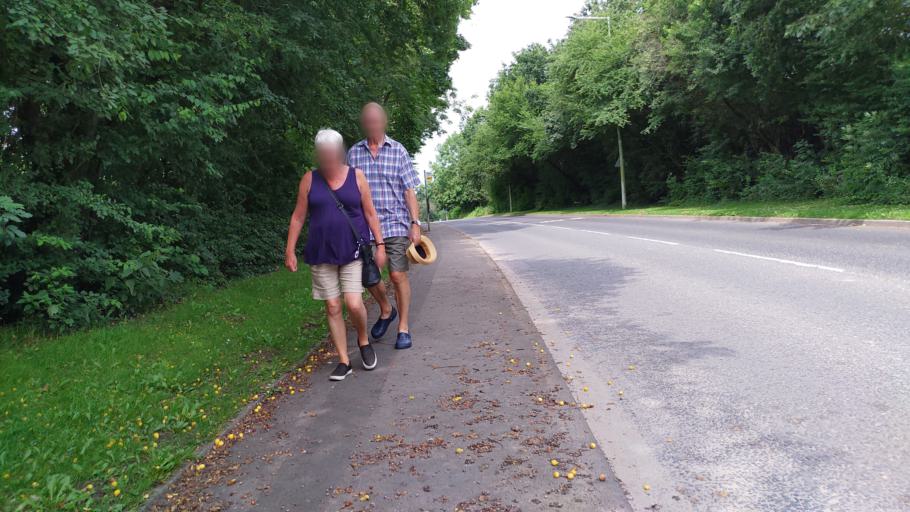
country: GB
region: England
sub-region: Lancashire
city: Coppull
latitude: 53.6339
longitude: -2.6363
